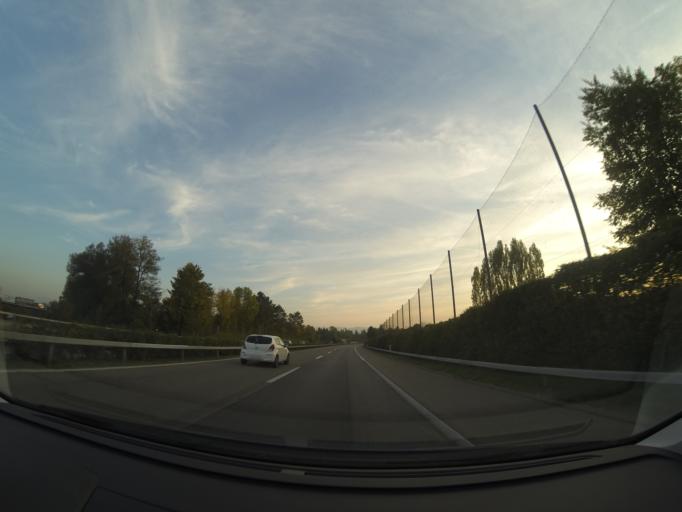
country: CH
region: Zurich
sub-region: Bezirk Hinwil
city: Bubikon
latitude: 47.2645
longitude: 8.8320
